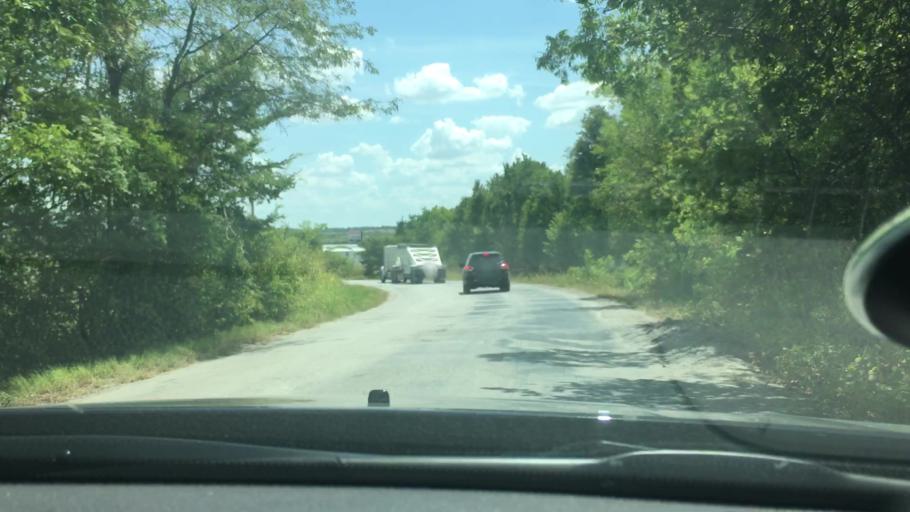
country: US
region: Oklahoma
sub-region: Carter County
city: Ardmore
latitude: 34.0785
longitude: -97.1541
